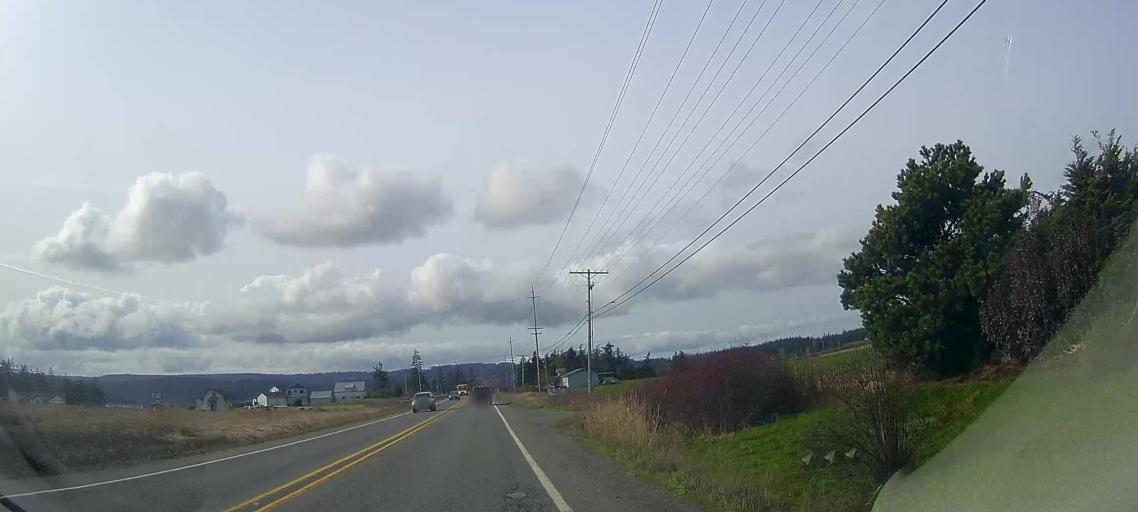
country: US
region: Washington
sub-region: Snohomish County
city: Stanwood
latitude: 48.2400
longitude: -122.4232
